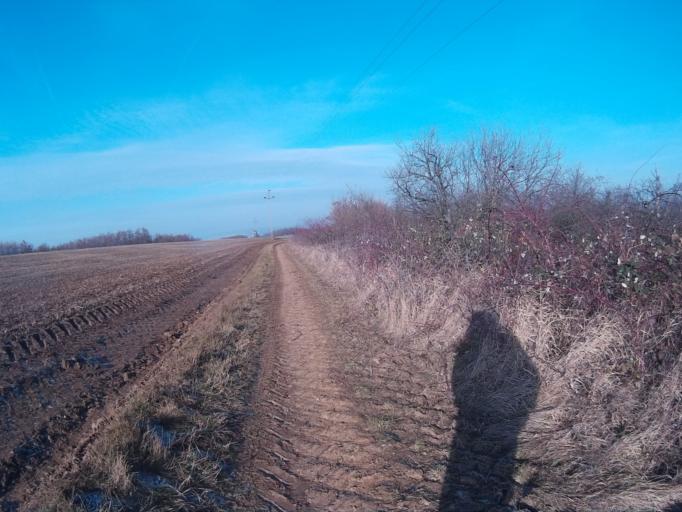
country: HU
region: Nograd
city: Bercel
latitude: 47.9353
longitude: 19.4286
